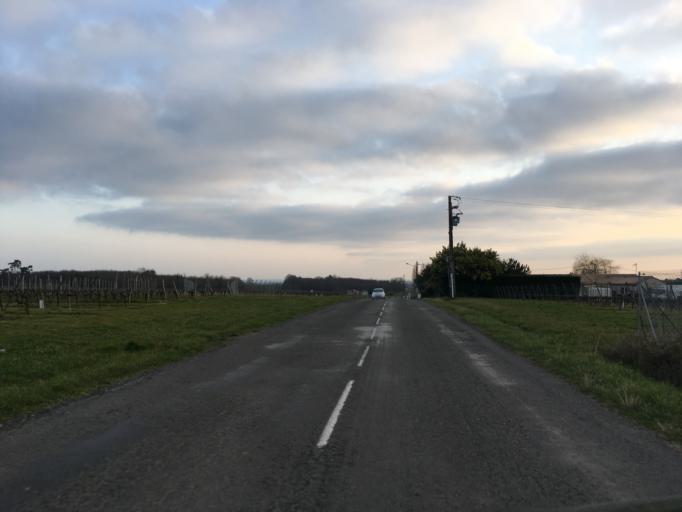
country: FR
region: Aquitaine
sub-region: Departement de la Gironde
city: Saint-Ciers-sur-Gironde
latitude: 45.3118
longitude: -0.5962
